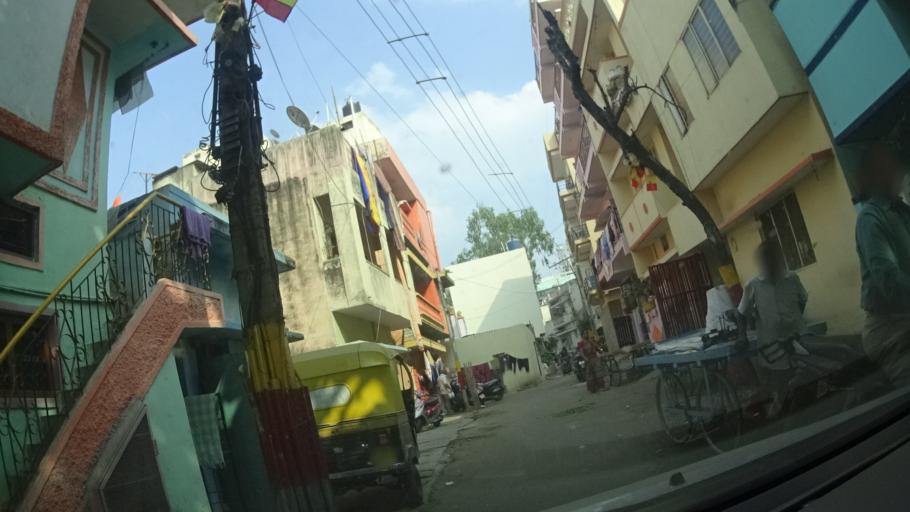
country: IN
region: Karnataka
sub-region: Bangalore Urban
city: Bangalore
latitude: 12.9465
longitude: 77.5612
